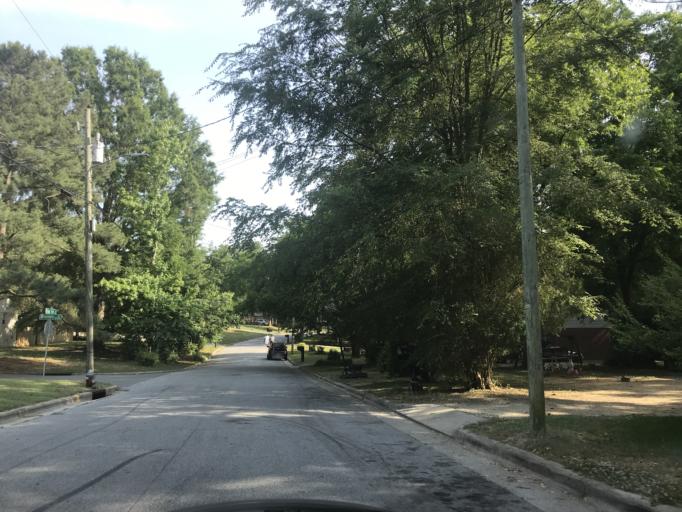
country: US
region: North Carolina
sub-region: Wake County
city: Raleigh
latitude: 35.7665
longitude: -78.5964
